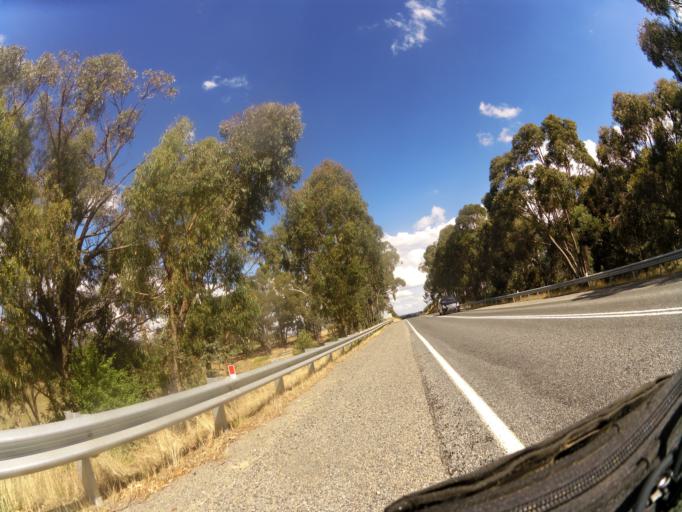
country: AU
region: Victoria
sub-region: Mansfield
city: Mansfield
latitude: -36.8887
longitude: 145.9954
